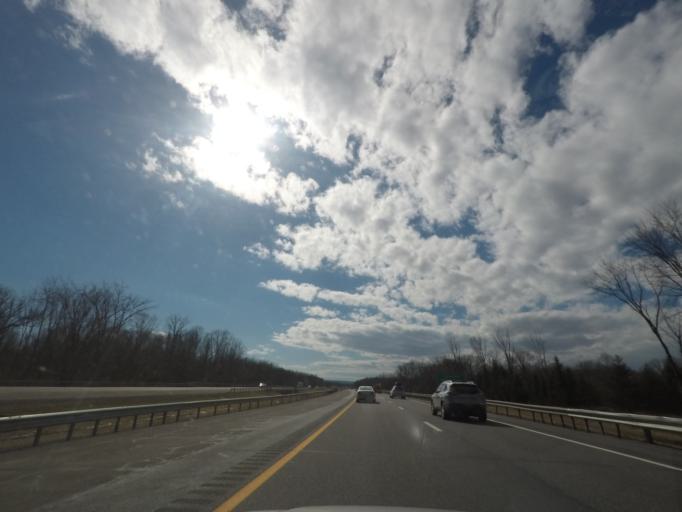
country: US
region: New York
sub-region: Madison County
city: Canastota
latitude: 43.1004
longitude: -75.7302
